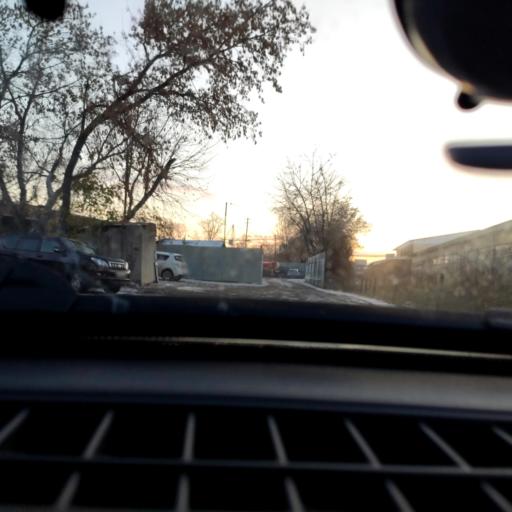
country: RU
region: Bashkortostan
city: Ufa
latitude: 54.8037
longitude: 56.0740
